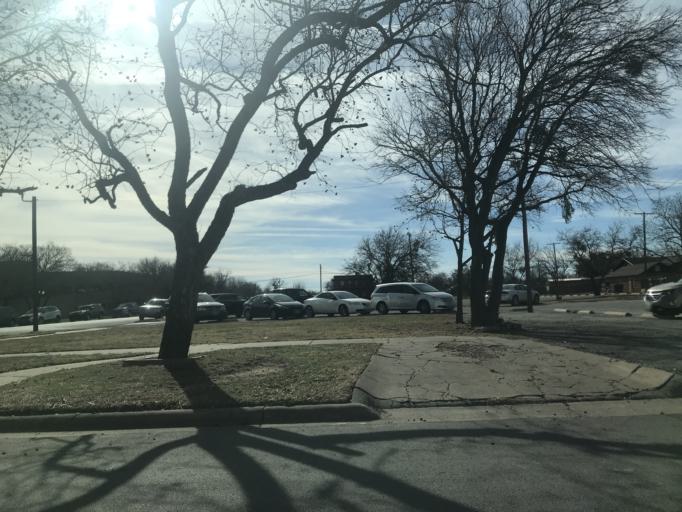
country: US
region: Texas
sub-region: Taylor County
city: Abilene
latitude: 32.4446
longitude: -99.7356
